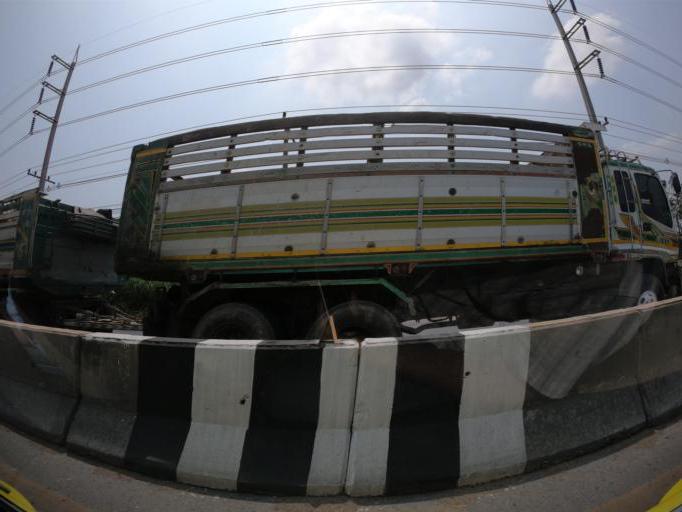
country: TH
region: Pathum Thani
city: Lam Luk Ka
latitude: 13.9374
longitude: 100.7554
